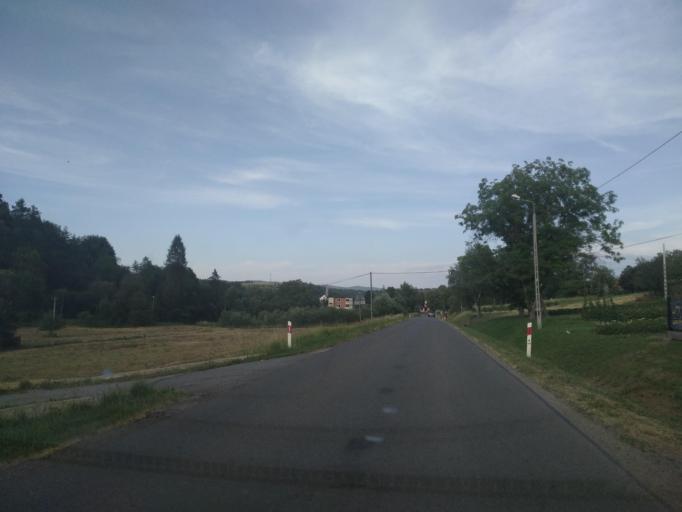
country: PL
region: Subcarpathian Voivodeship
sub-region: Powiat sanocki
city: Zagorz
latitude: 49.5017
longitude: 22.2575
